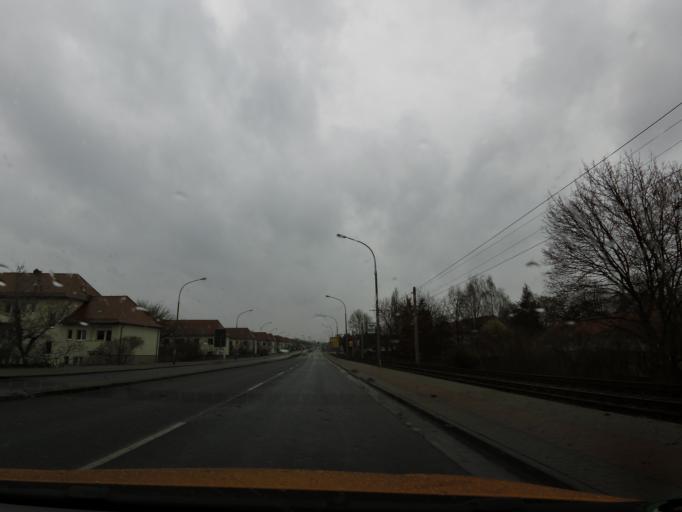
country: DE
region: Brandenburg
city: Brandenburg an der Havel
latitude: 52.4130
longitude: 12.5271
